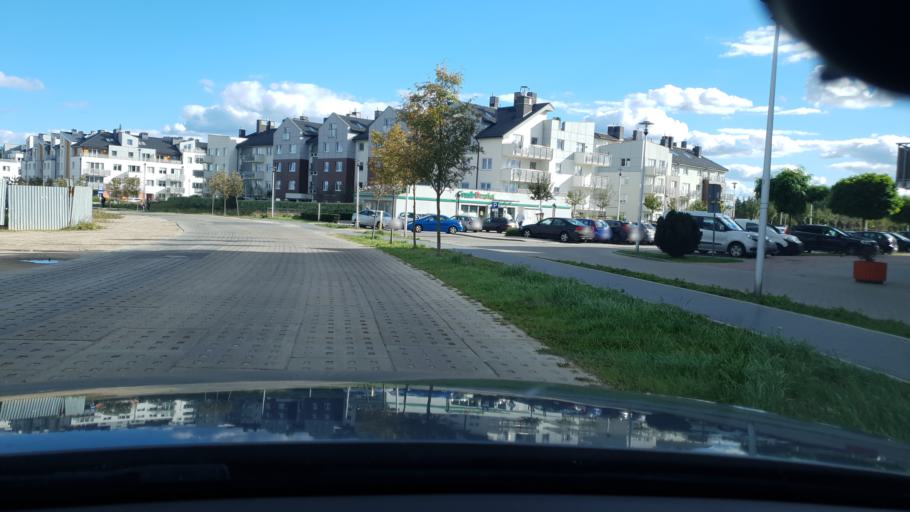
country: PL
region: Pomeranian Voivodeship
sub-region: Powiat kartuski
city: Chwaszczyno
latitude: 54.4934
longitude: 18.4324
